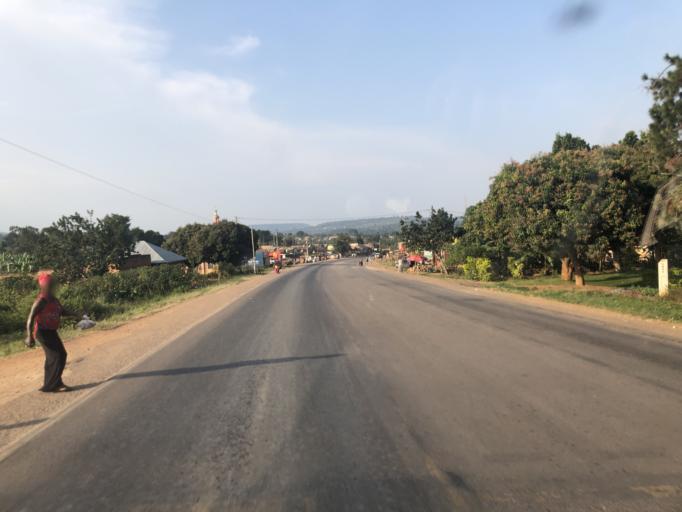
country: UG
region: Central Region
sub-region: Butambala District
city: Gombe
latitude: 0.1171
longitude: 32.1807
